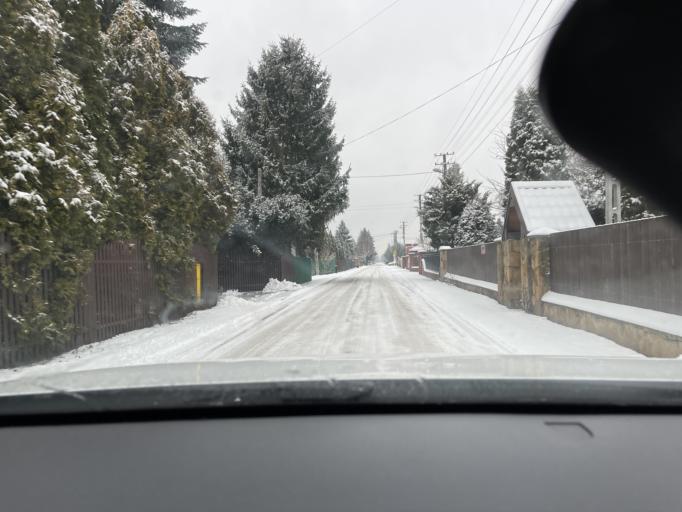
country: PL
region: Masovian Voivodeship
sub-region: Powiat zyrardowski
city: Zyrardow
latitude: 52.0296
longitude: 20.4603
